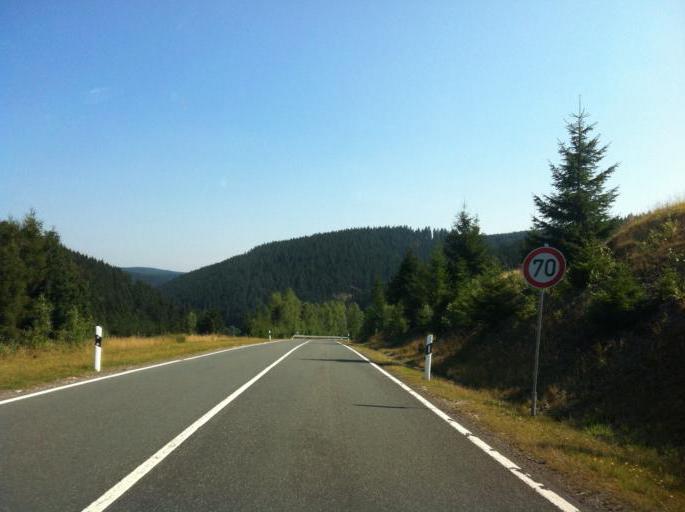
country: DE
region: Thuringia
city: Goldisthal
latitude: 50.5219
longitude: 11.0089
